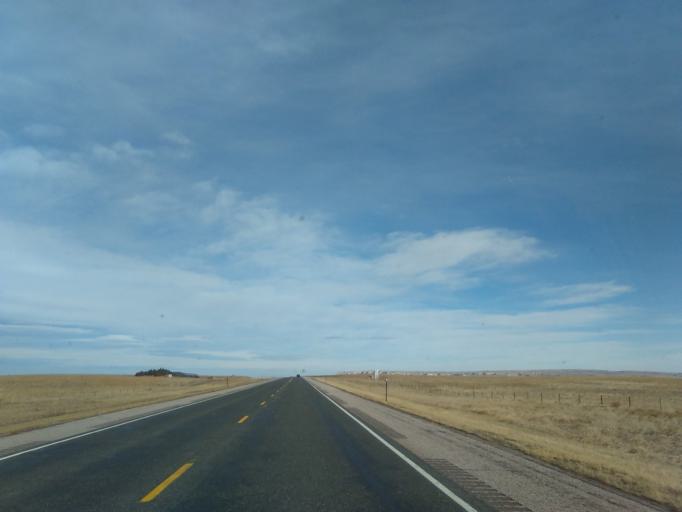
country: US
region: Wyoming
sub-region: Goshen County
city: Torrington
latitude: 41.6081
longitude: -104.2560
